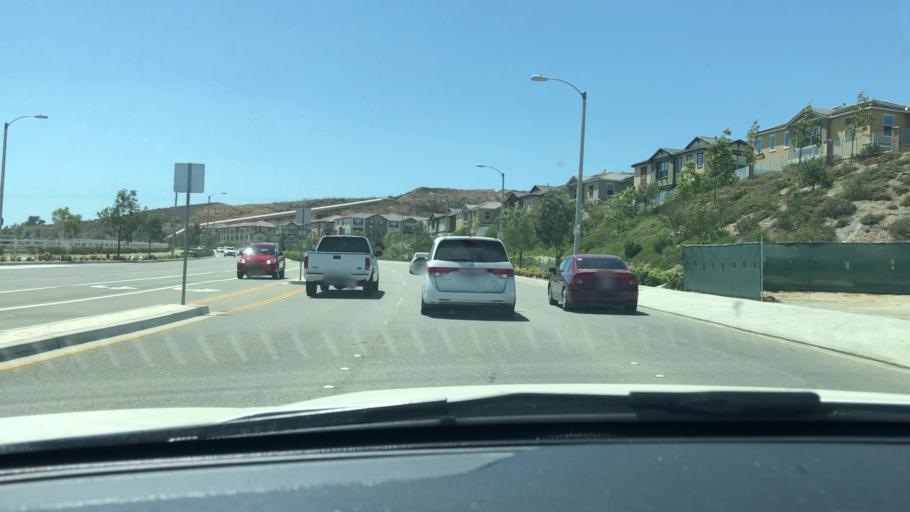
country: US
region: California
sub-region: Los Angeles County
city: Santa Clarita
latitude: 34.4272
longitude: -118.5076
